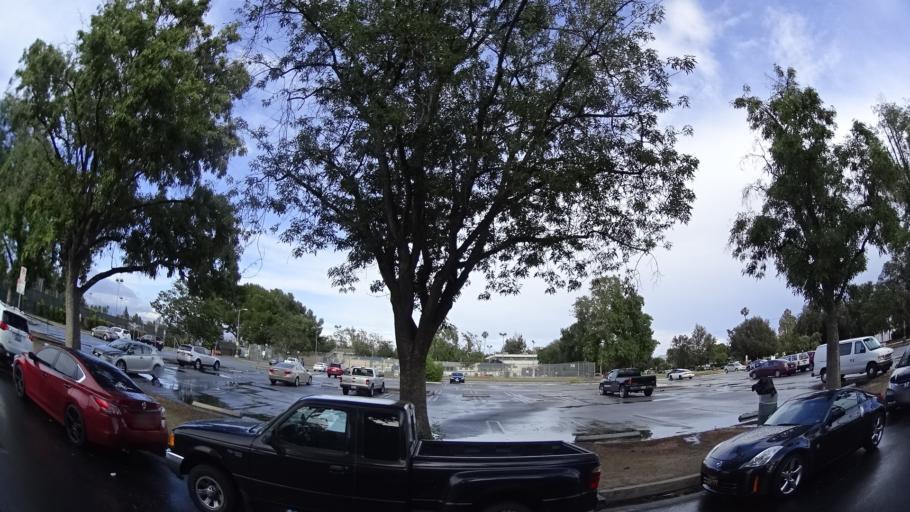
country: US
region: California
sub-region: Los Angeles County
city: Sherman Oaks
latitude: 34.1603
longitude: -118.4443
